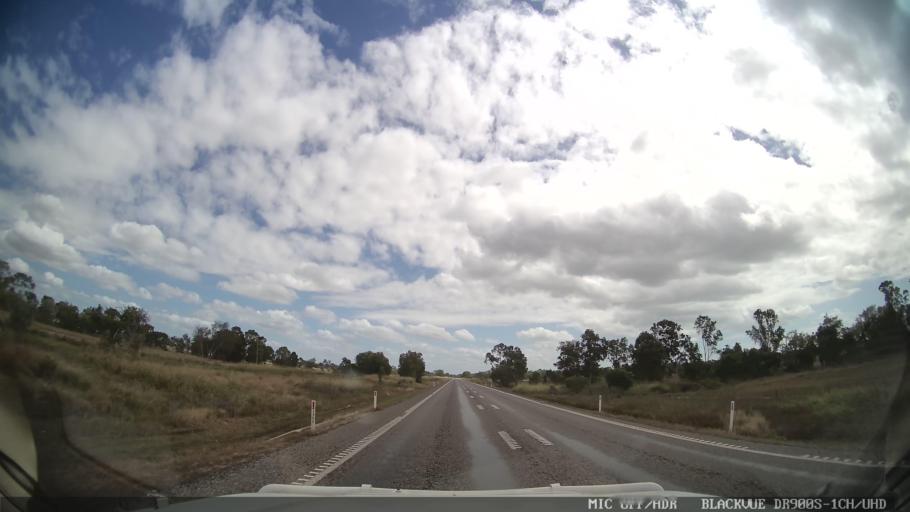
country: AU
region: Queensland
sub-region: Burdekin
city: Home Hill
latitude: -19.9055
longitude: 147.7694
